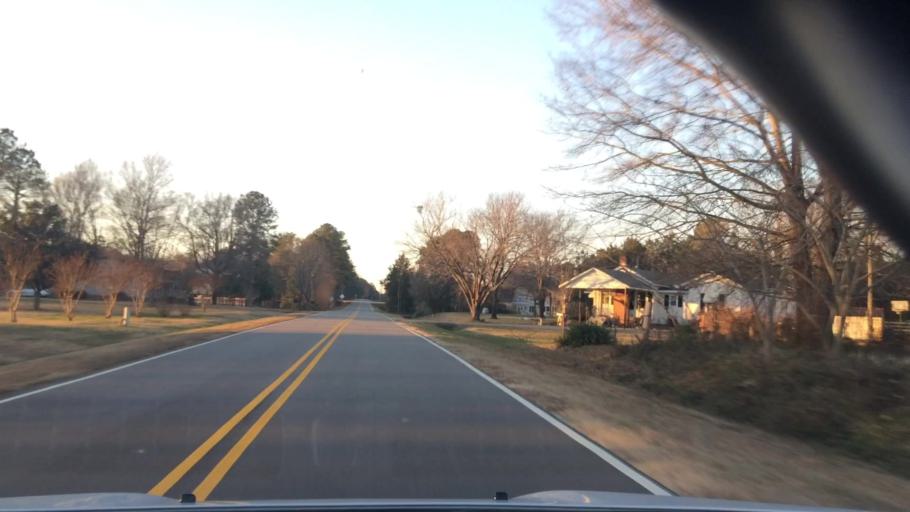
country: US
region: North Carolina
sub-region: Wake County
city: Rolesville
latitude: 35.9423
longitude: -78.4043
